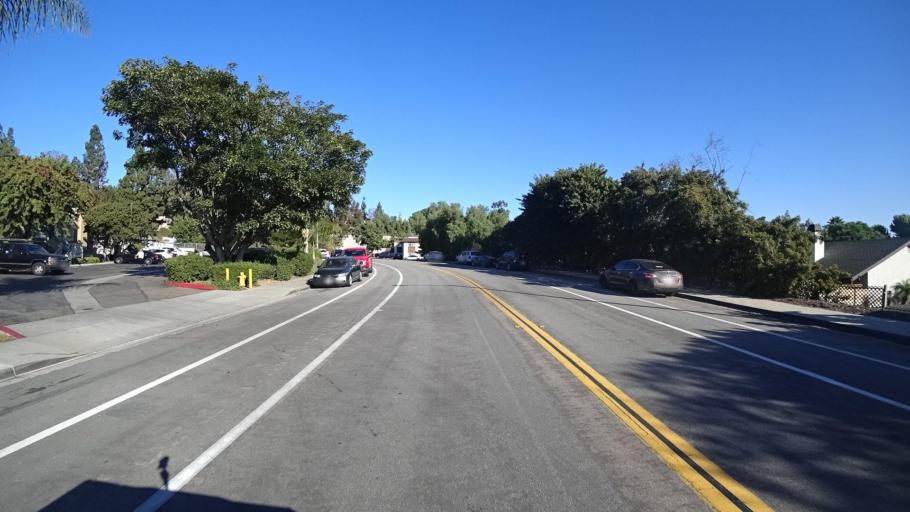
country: US
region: California
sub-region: San Diego County
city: Bonita
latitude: 32.6814
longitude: -117.0271
